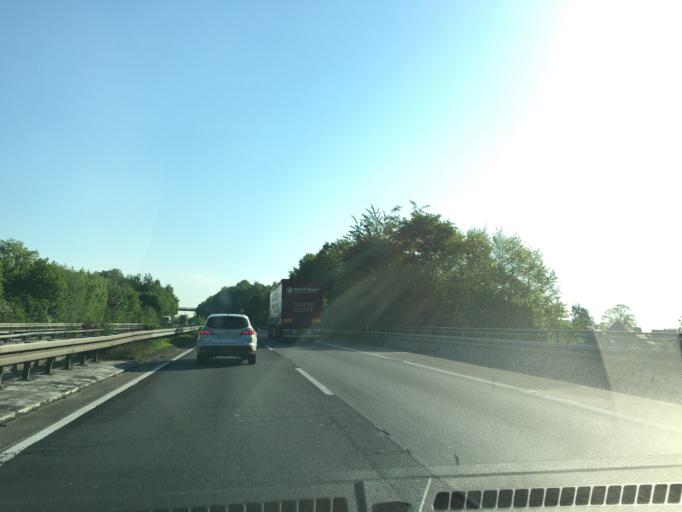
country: DE
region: Lower Saxony
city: Hasbergen
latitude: 52.2476
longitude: 7.9082
